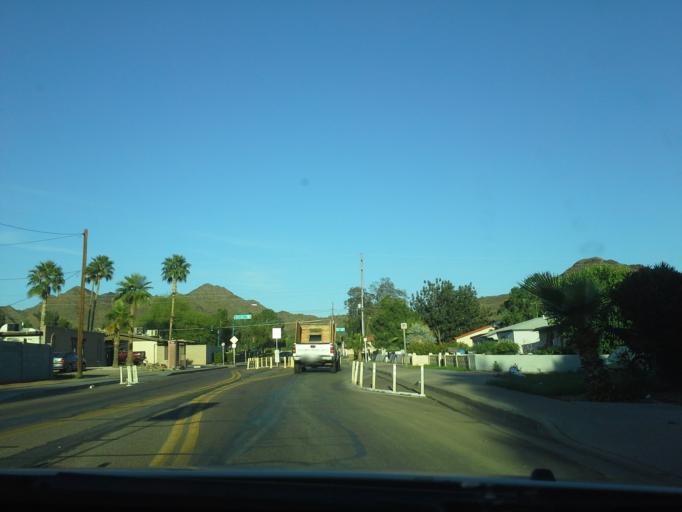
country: US
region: Arizona
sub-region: Maricopa County
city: Paradise Valley
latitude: 33.5713
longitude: -112.0580
